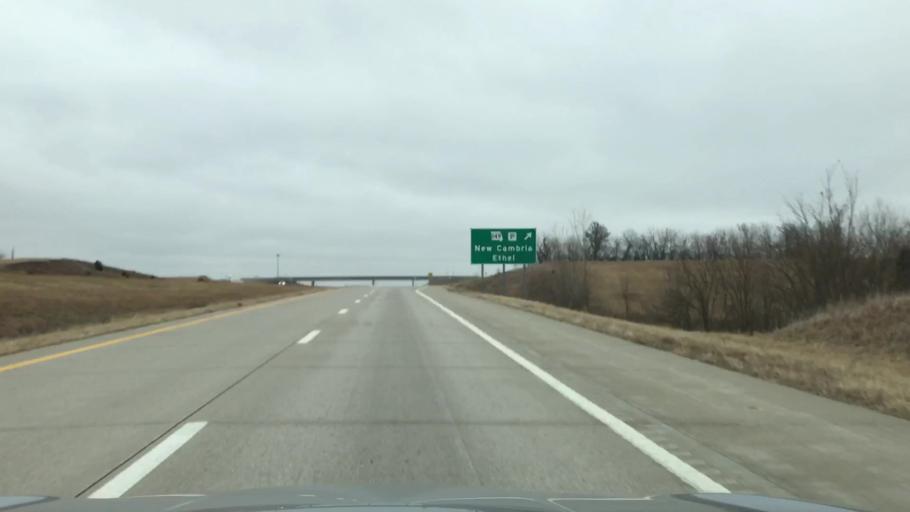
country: US
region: Missouri
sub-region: Linn County
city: Marceline
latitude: 39.7650
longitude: -92.7560
